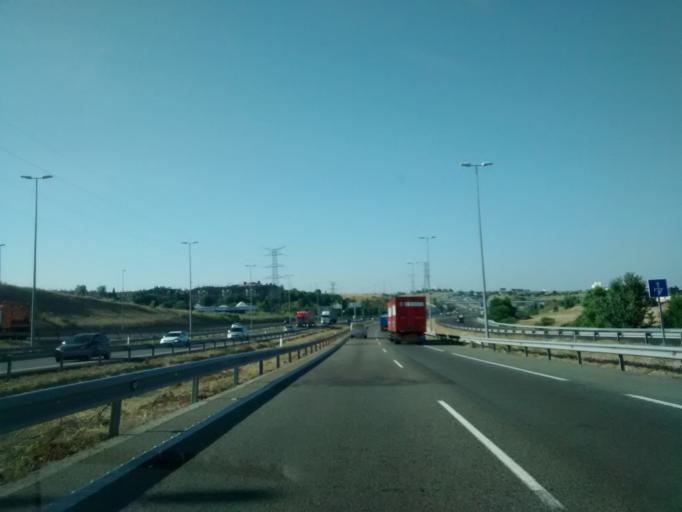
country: ES
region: Madrid
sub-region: Provincia de Madrid
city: Las Rozas de Madrid
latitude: 40.4946
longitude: -3.8947
